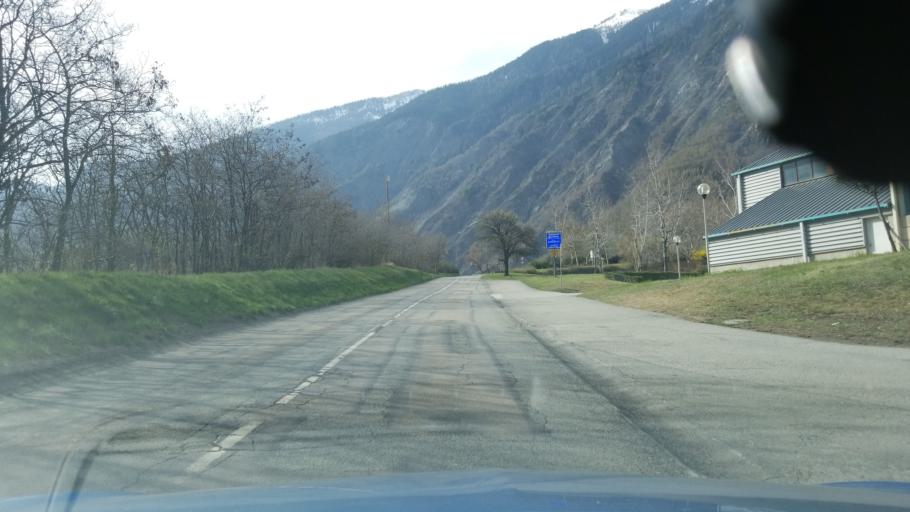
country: FR
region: Rhone-Alpes
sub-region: Departement de la Savoie
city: Villargondran
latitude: 45.2622
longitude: 6.3831
